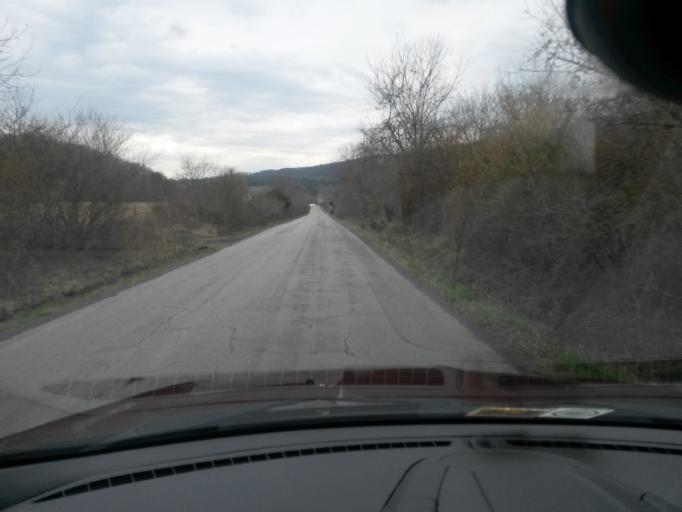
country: US
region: Virginia
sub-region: Bath County
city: Warm Springs
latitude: 38.0513
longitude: -79.8549
